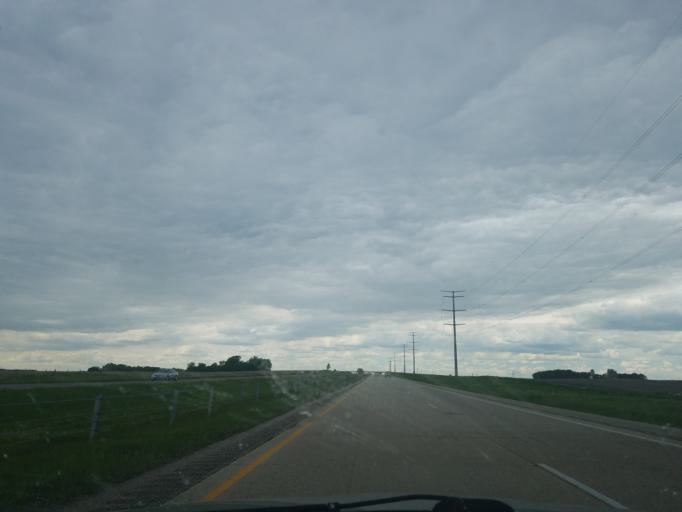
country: US
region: Minnesota
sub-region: Douglas County
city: Alexandria
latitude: 45.9656
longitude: -95.6343
